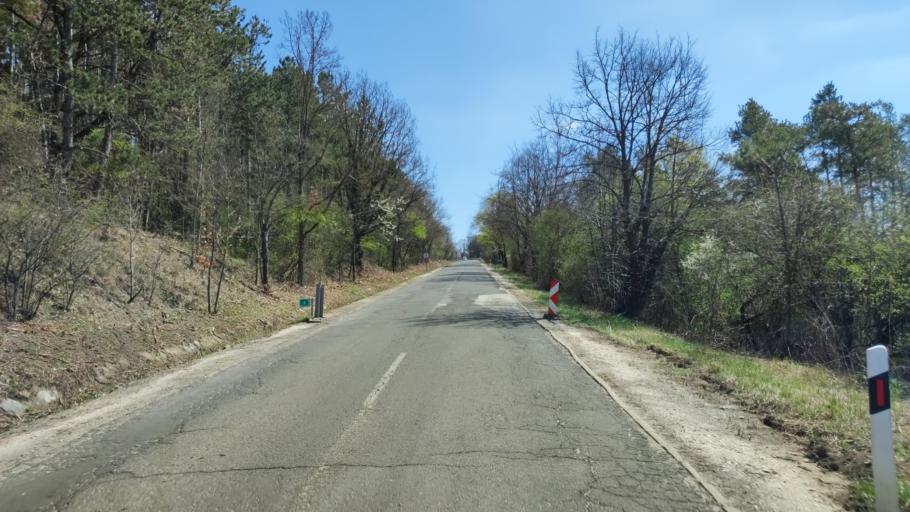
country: HU
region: Pest
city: Kosd
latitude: 47.7949
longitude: 19.1711
